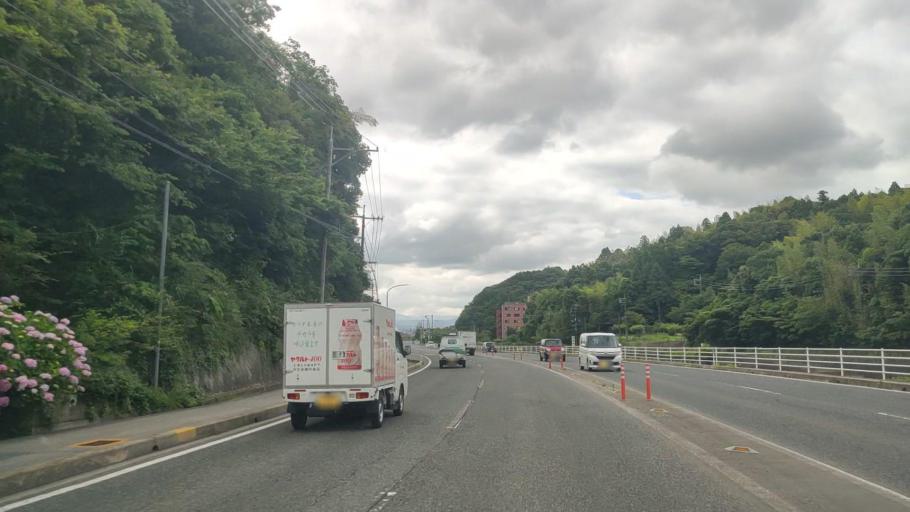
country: JP
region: Tottori
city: Yonago
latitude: 35.4133
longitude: 133.3546
